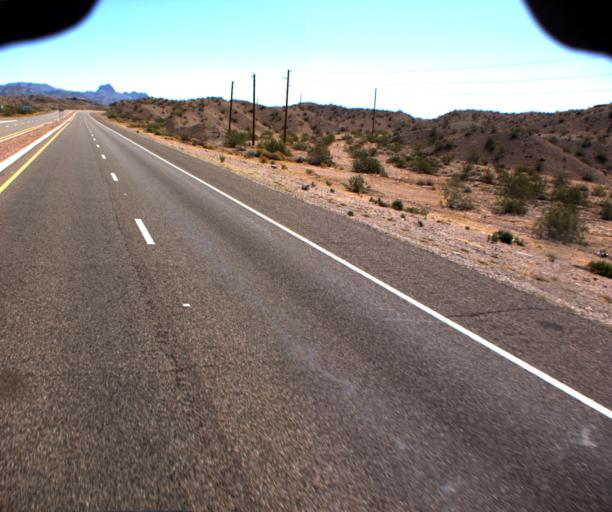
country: US
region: Nevada
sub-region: Clark County
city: Laughlin
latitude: 35.1877
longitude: -114.5459
